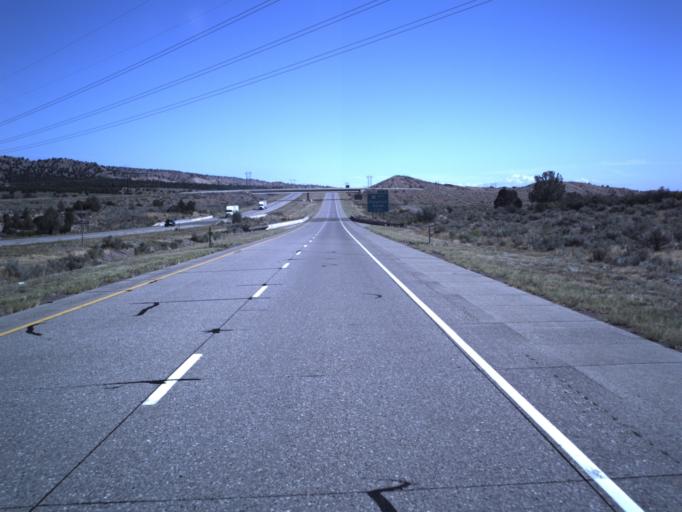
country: US
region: Utah
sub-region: Sevier County
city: Monroe
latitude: 38.5856
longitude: -112.2745
